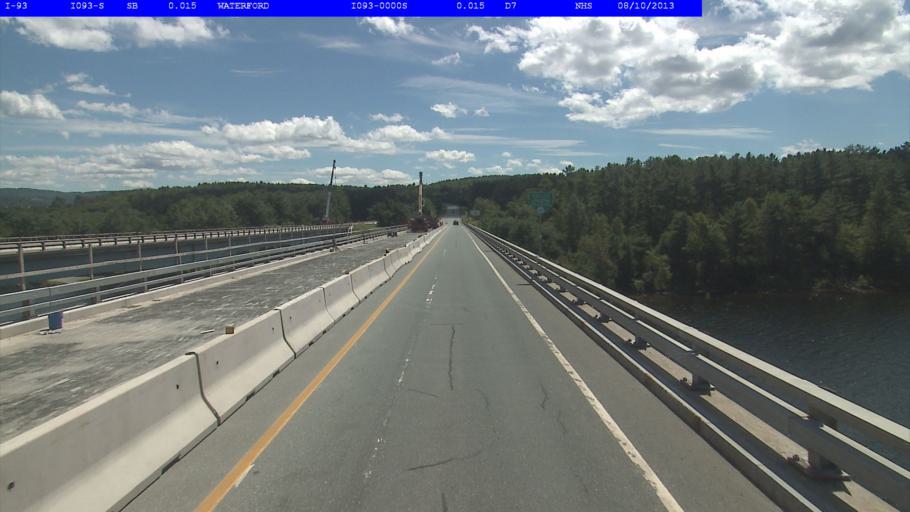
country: US
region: New Hampshire
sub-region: Grafton County
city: Littleton
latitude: 44.3434
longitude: -71.8914
